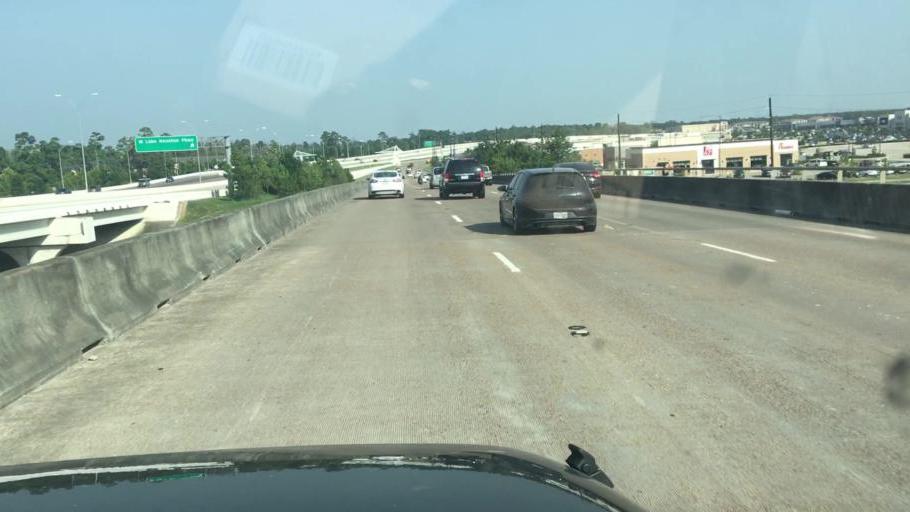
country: US
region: Texas
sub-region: Harris County
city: Atascocita
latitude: 29.9310
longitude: -95.2059
